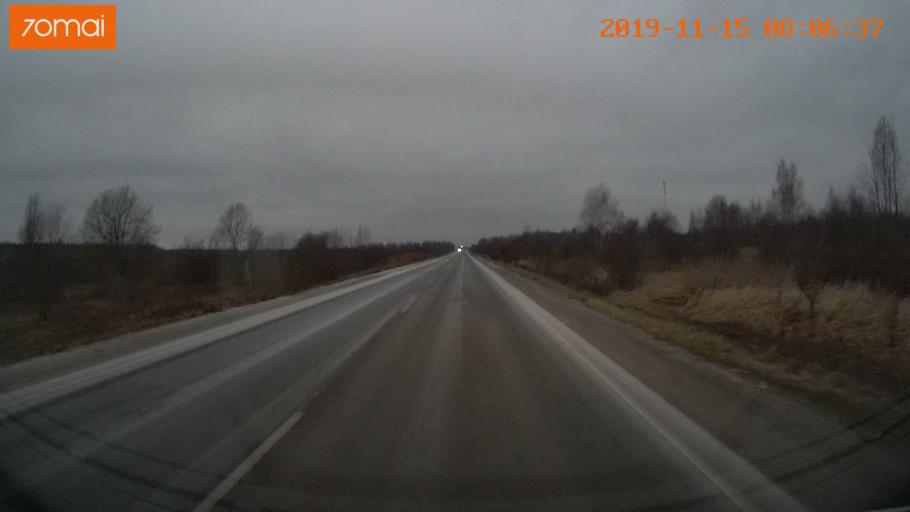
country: RU
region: Vologda
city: Cherepovets
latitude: 59.0231
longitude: 38.0339
